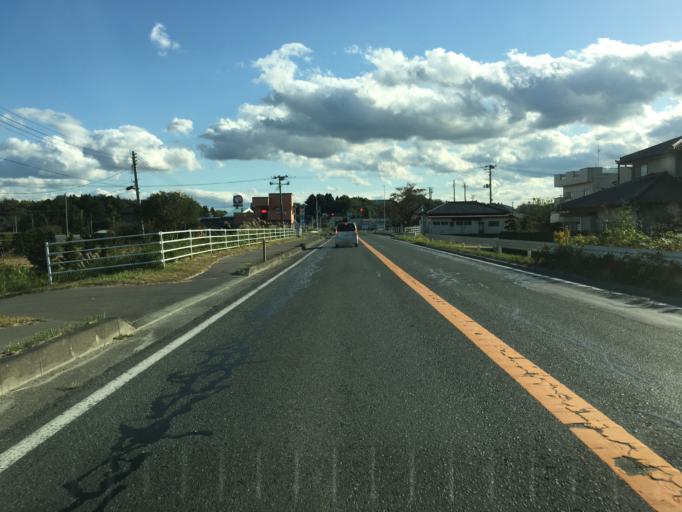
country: JP
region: Miyagi
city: Marumori
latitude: 37.8704
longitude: 140.9193
